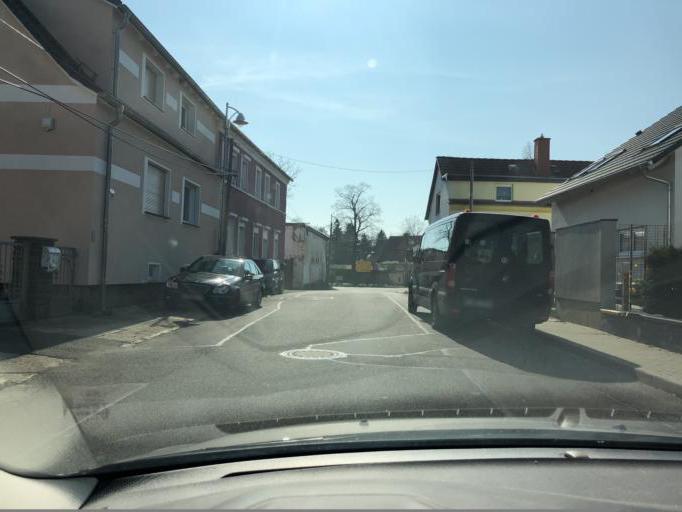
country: DE
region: Saxony
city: Rackwitz
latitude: 51.4205
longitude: 12.4220
